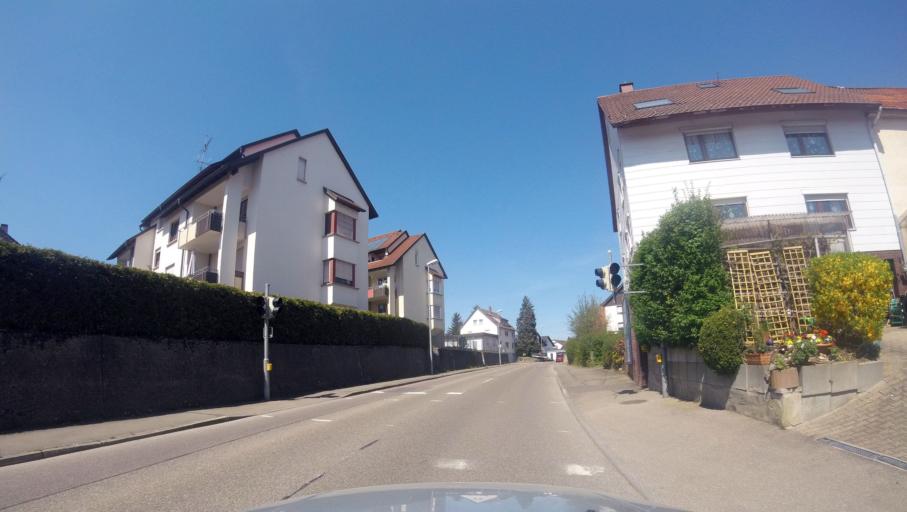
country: DE
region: Baden-Wuerttemberg
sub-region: Regierungsbezirk Stuttgart
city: Mutlangen
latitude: 48.8261
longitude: 9.7955
